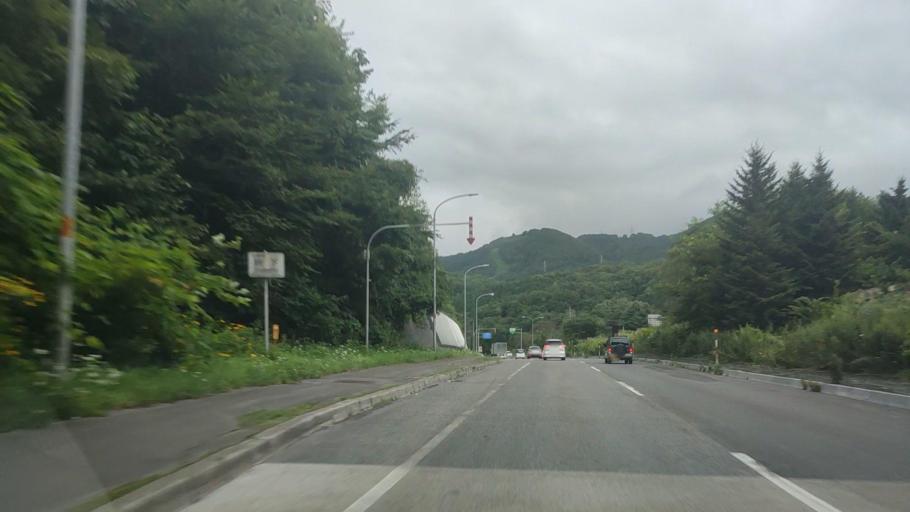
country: JP
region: Hokkaido
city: Nanae
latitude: 41.9499
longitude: 140.6446
